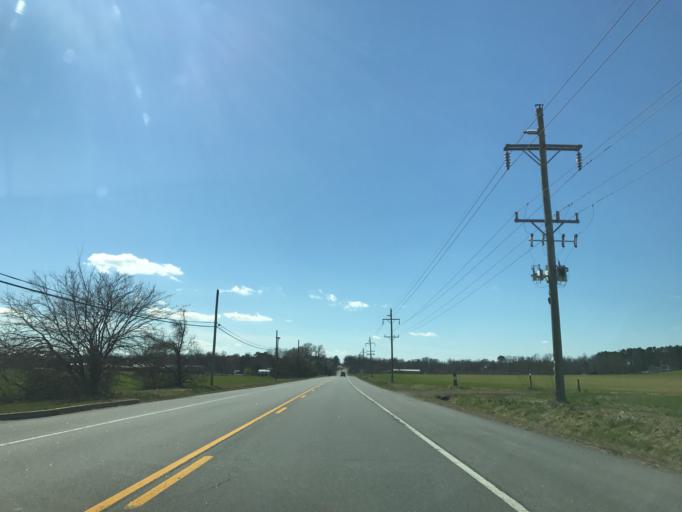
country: US
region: Maryland
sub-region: Queen Anne's County
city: Kingstown
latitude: 39.2286
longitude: -76.0521
